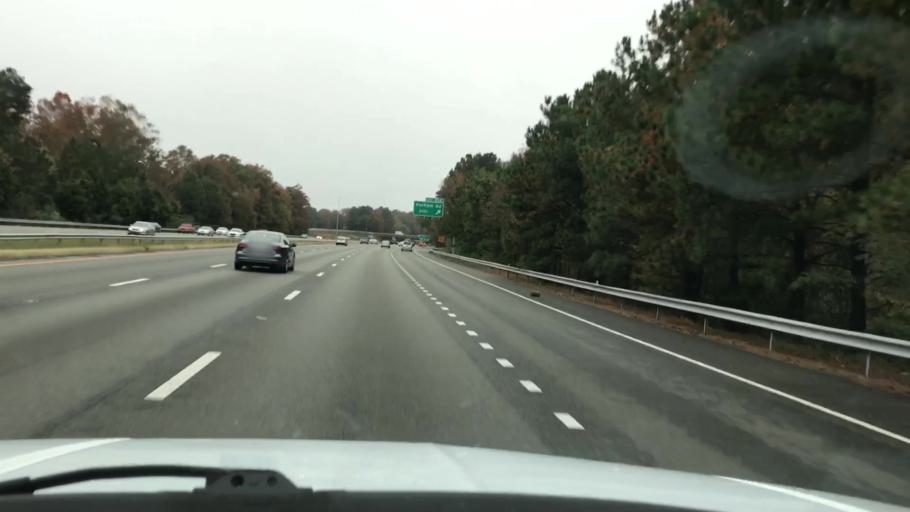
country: US
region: Virginia
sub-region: Henrico County
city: Chamberlayne
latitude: 37.6308
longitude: -77.4495
